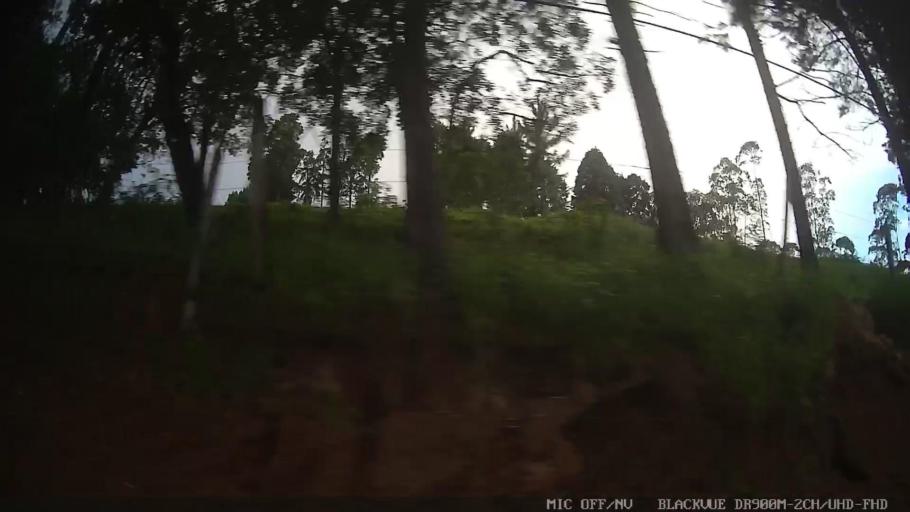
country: BR
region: Sao Paulo
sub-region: Ribeirao Pires
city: Ribeirao Pires
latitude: -23.6705
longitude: -46.3181
